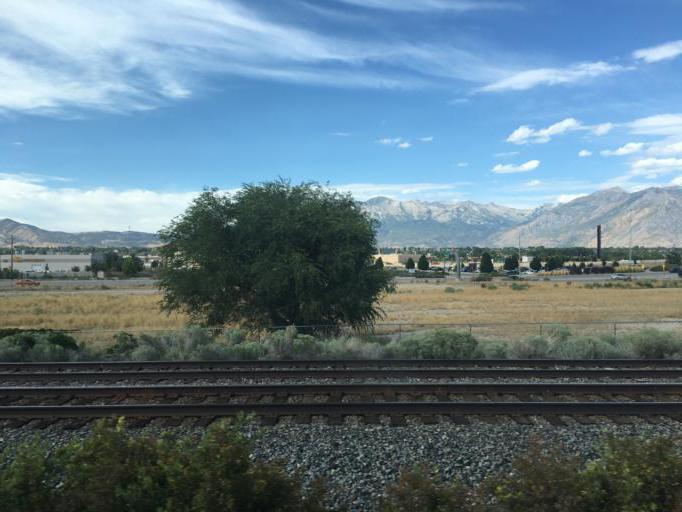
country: US
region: Utah
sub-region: Utah County
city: American Fork
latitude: 40.3755
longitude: -111.8236
